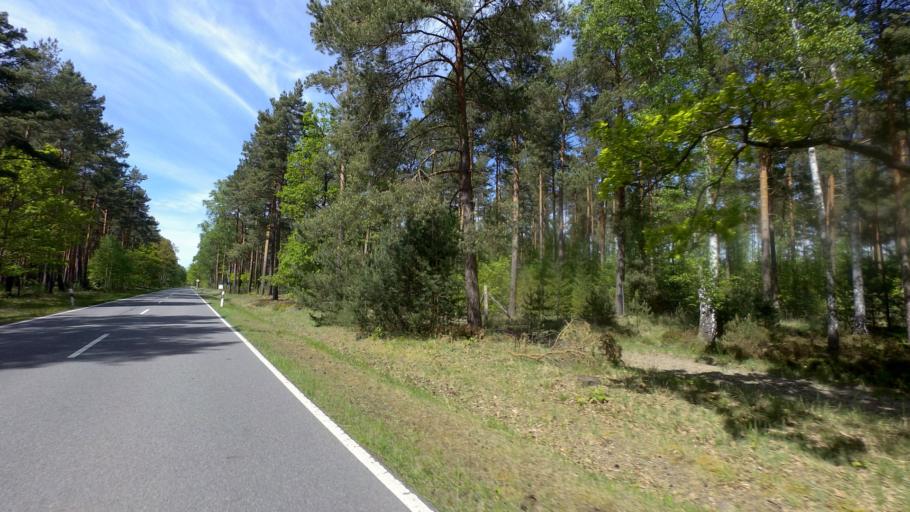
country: DE
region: Brandenburg
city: Sperenberg
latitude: 52.0932
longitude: 13.3825
